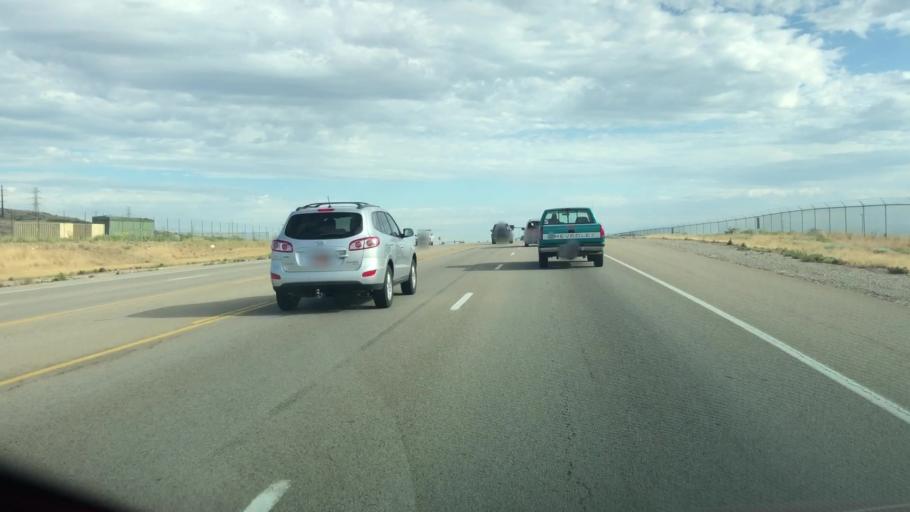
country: US
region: Utah
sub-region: Salt Lake County
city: Bluffdale
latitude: 40.4308
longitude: -111.9278
